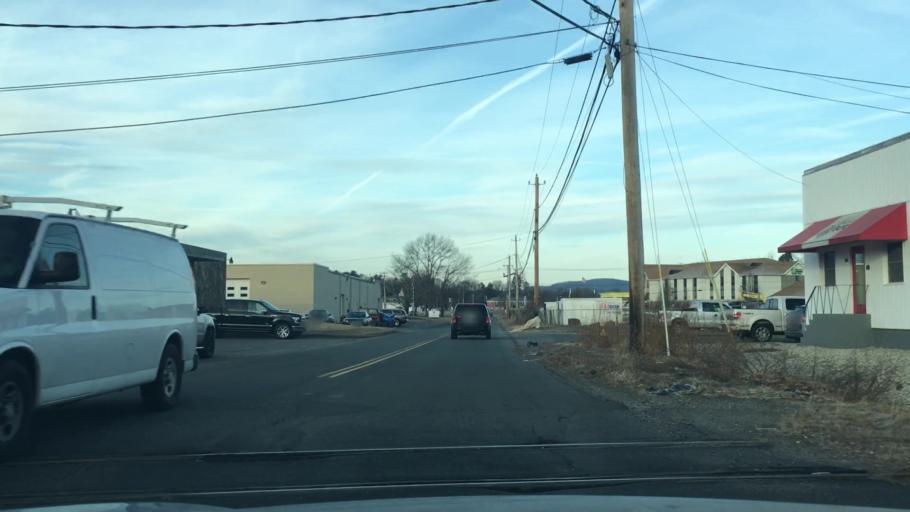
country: US
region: Massachusetts
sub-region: Hampden County
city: Westfield
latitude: 42.1413
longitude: -72.7275
